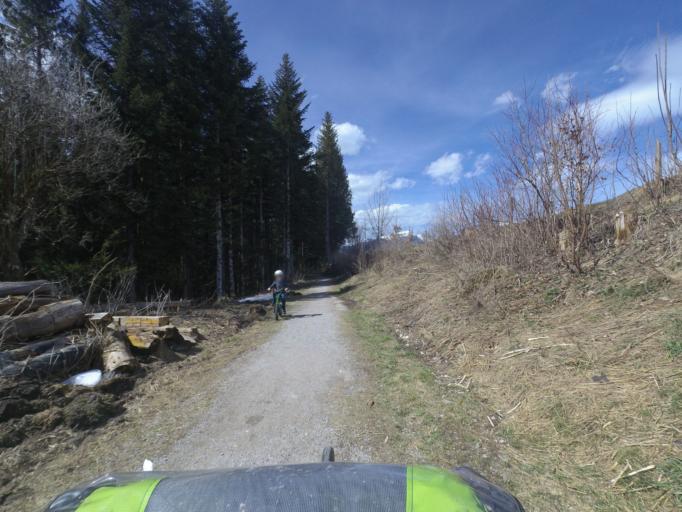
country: AT
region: Salzburg
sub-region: Politischer Bezirk Hallein
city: Abtenau
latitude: 47.5619
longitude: 13.3433
